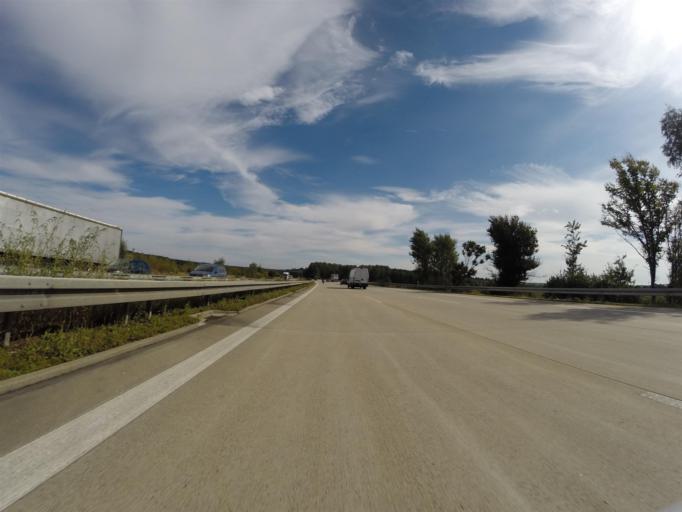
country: DE
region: Saxony
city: Rosswein
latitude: 51.0010
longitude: 13.2098
